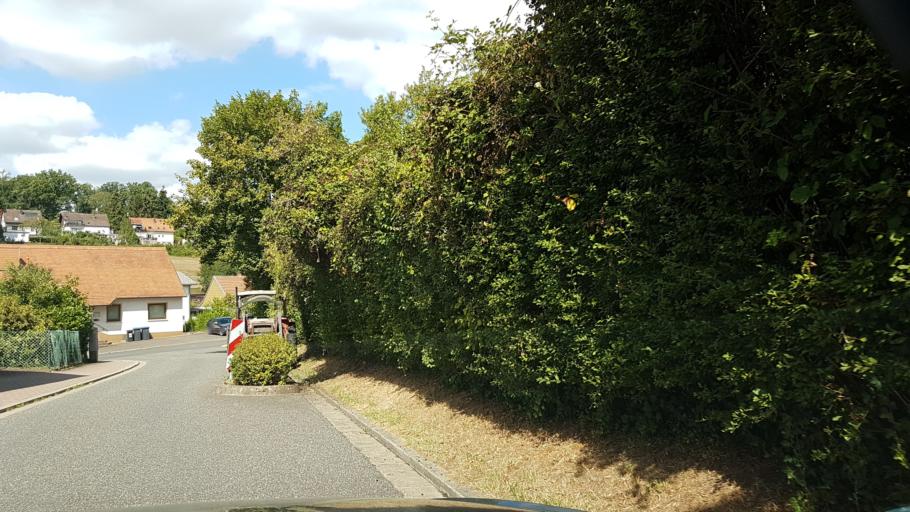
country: DE
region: Saarland
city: Bexbach
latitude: 49.3198
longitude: 7.2858
